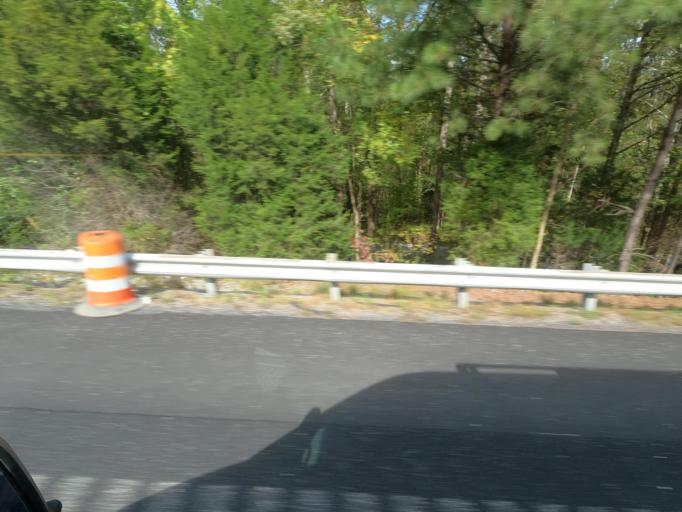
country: US
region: Tennessee
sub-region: Decatur County
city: Parsons
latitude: 35.8223
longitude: -88.1333
